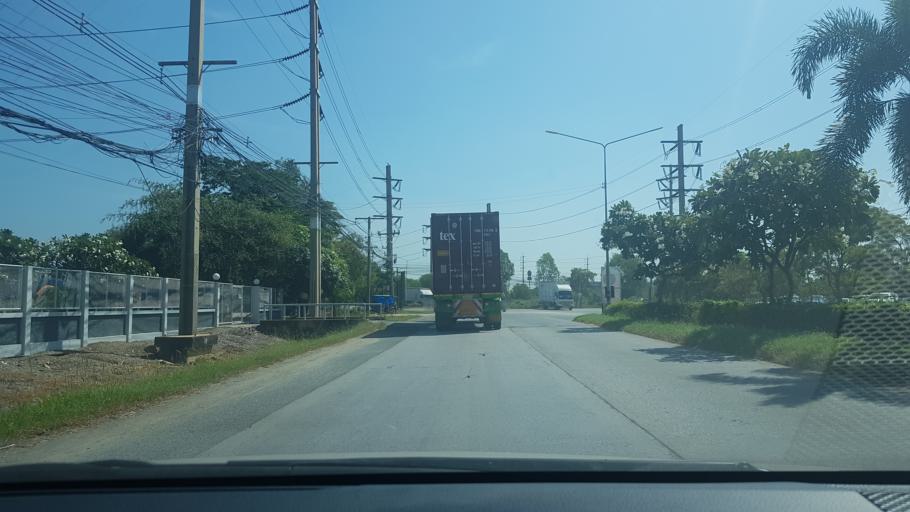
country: TH
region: Phra Nakhon Si Ayutthaya
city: Bang Pa-in
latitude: 14.2495
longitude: 100.6104
